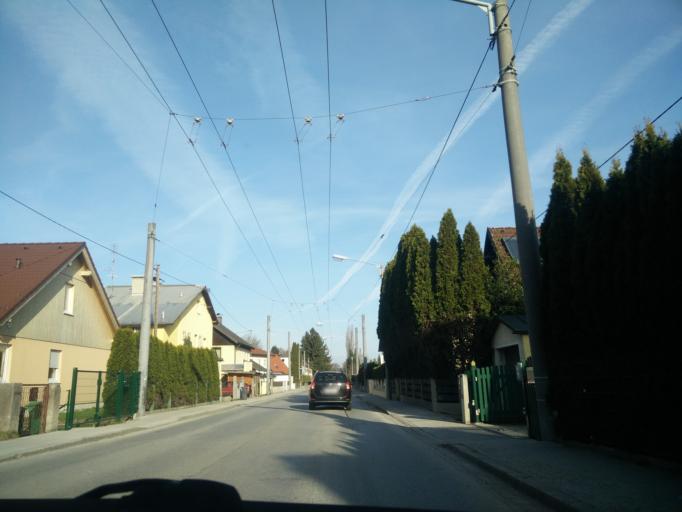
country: AT
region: Salzburg
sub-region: Politischer Bezirk Salzburg-Umgebung
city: Bergheim
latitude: 47.8180
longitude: 13.0247
